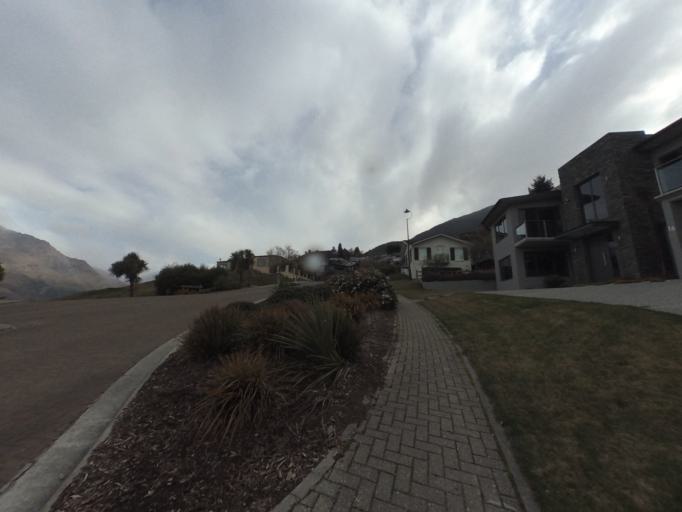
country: NZ
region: Otago
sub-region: Queenstown-Lakes District
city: Queenstown
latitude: -45.0402
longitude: 168.6353
